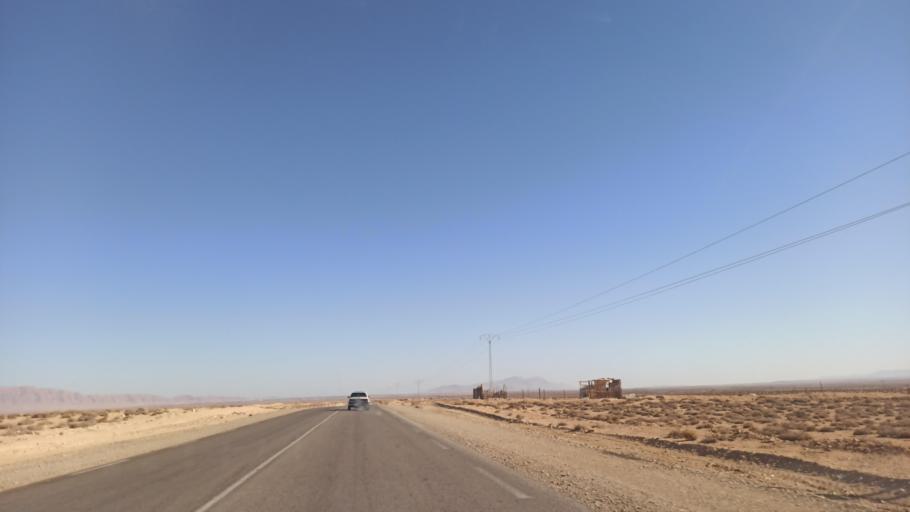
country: TN
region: Gafsa
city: Al Metlaoui
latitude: 34.3289
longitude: 8.5478
